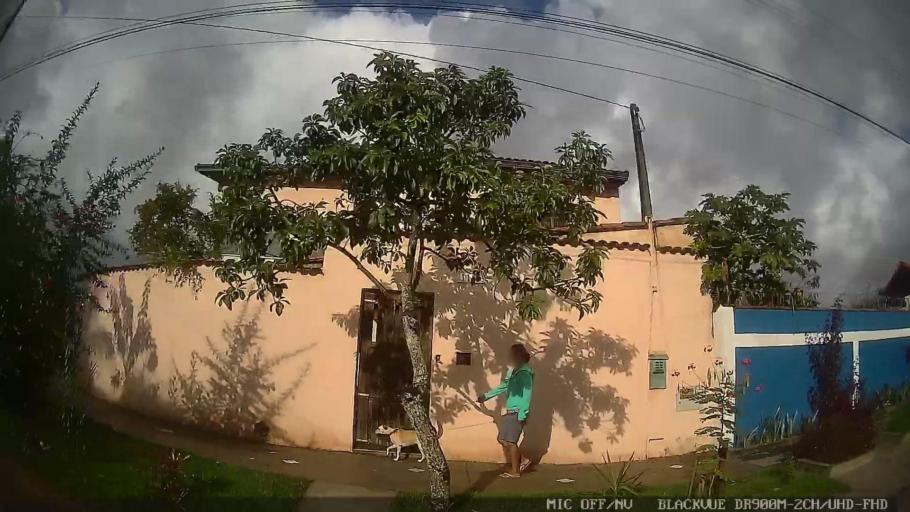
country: BR
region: Sao Paulo
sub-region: Itanhaem
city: Itanhaem
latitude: -24.1975
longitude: -46.8681
